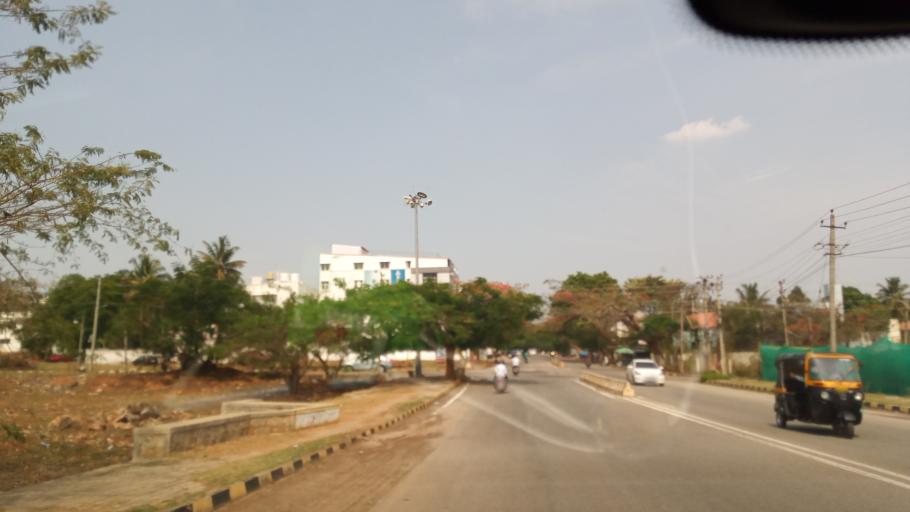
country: IN
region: Karnataka
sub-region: Mysore
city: Mysore
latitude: 12.2873
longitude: 76.6189
